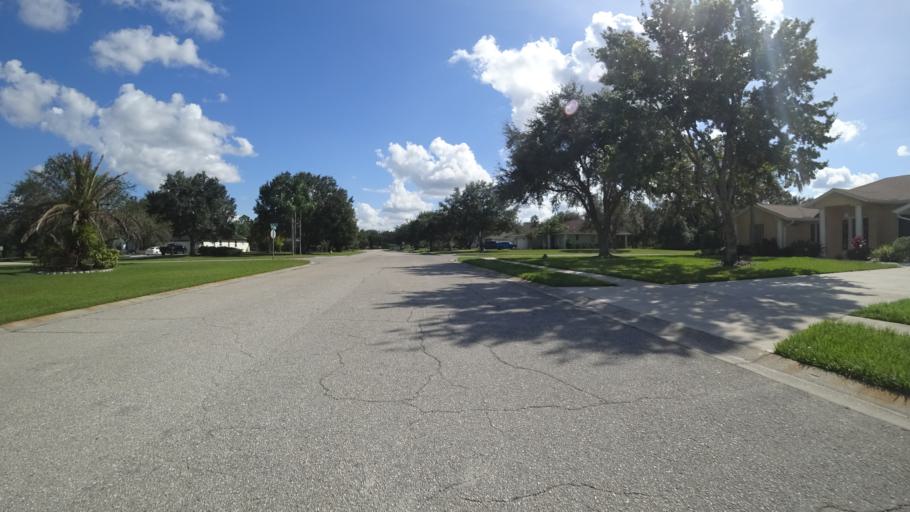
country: US
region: Florida
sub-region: Manatee County
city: Ellenton
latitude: 27.4949
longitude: -82.3961
